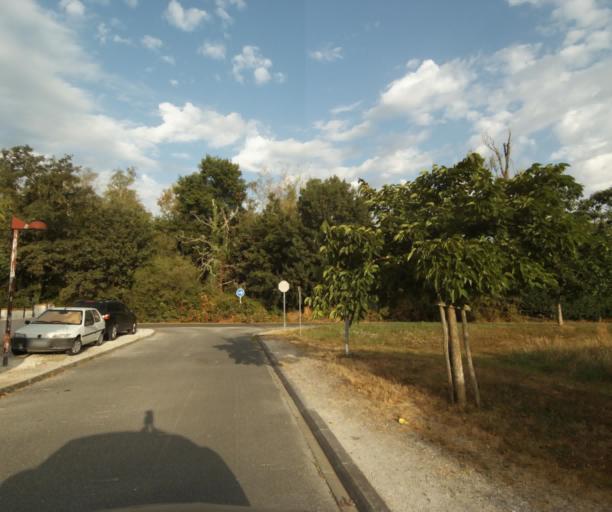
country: FR
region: Aquitaine
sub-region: Departement de la Gironde
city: Creon
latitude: 44.7799
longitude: -0.3494
